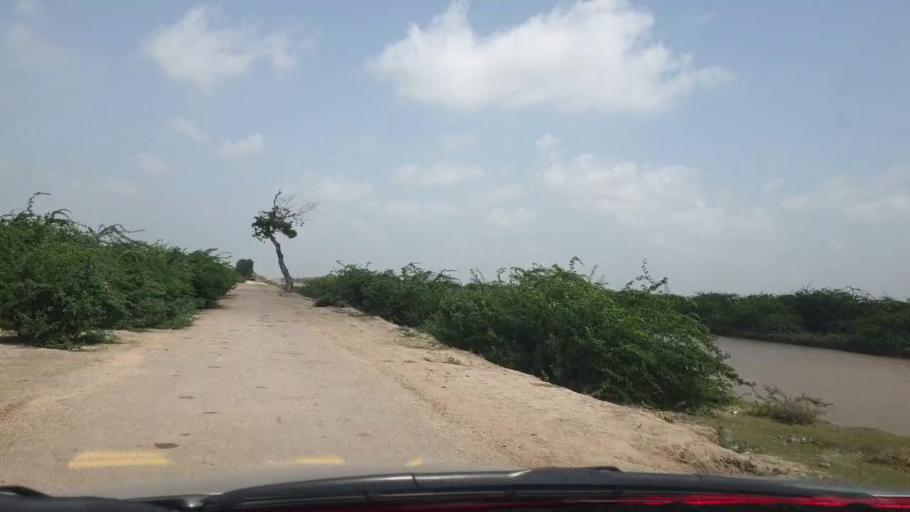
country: PK
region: Sindh
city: Talhar
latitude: 24.8922
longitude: 68.8353
